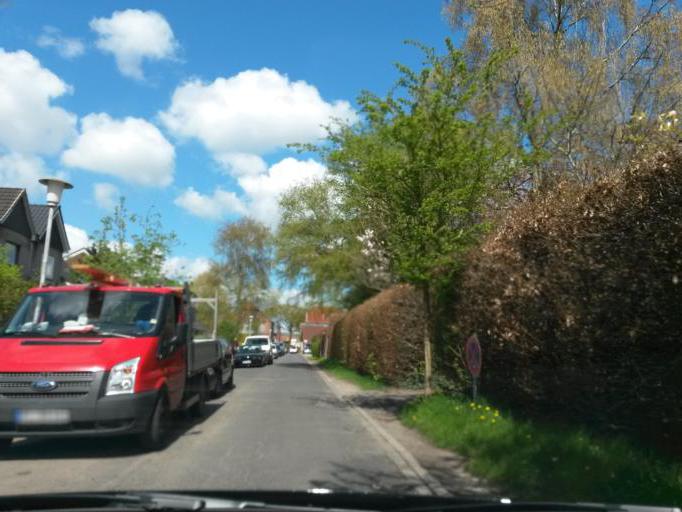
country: DE
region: Schleswig-Holstein
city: Uetersen
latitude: 53.6812
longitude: 9.6532
